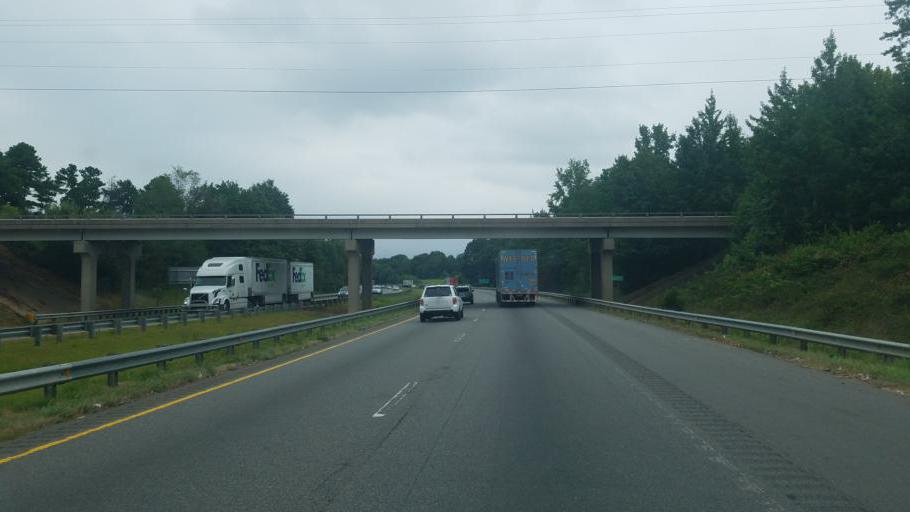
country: US
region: North Carolina
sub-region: Iredell County
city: Troutman
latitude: 35.6801
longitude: -80.8533
